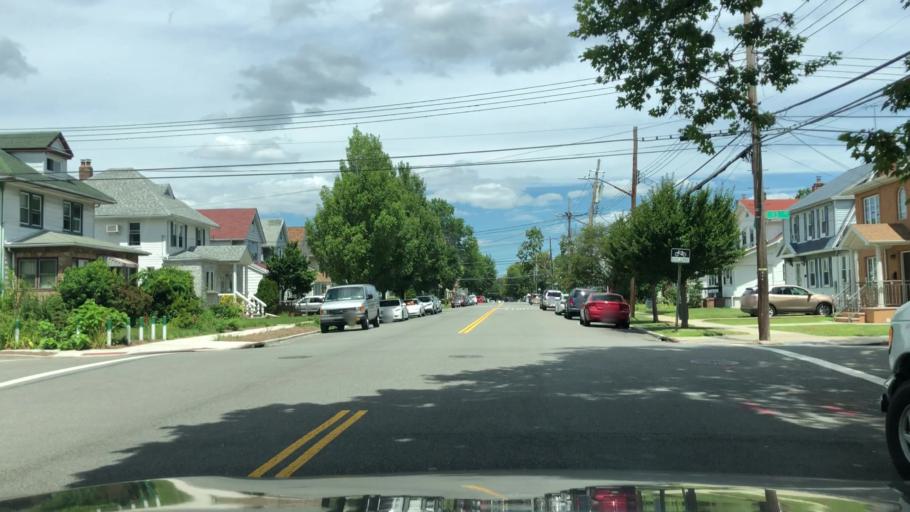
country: US
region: New York
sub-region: Nassau County
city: Bellerose Terrace
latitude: 40.7224
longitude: -73.7332
